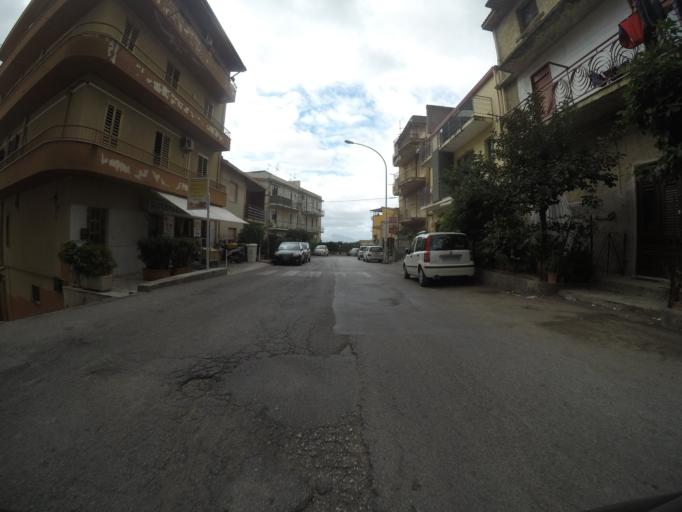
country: IT
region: Sicily
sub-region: Palermo
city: Montelepre
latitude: 38.0925
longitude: 13.1735
